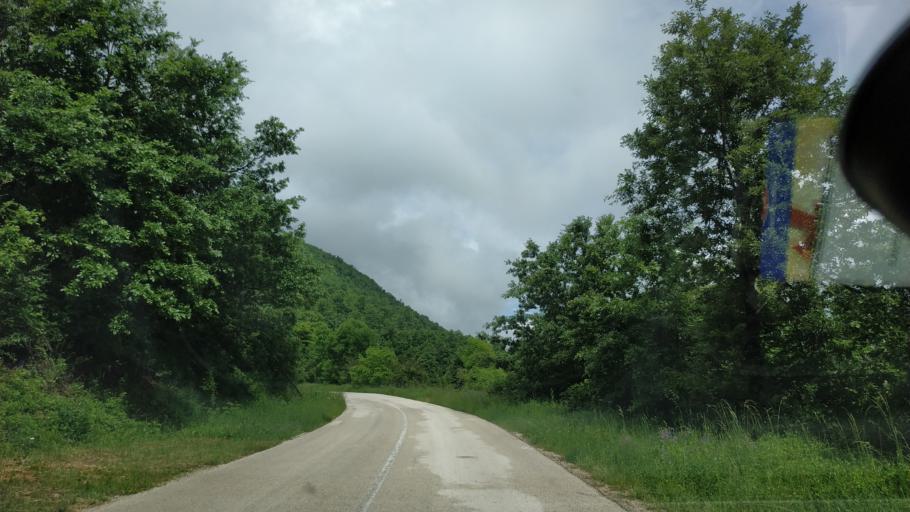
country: RS
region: Central Serbia
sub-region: Zajecarski Okrug
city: Boljevac
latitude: 43.7358
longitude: 21.9524
